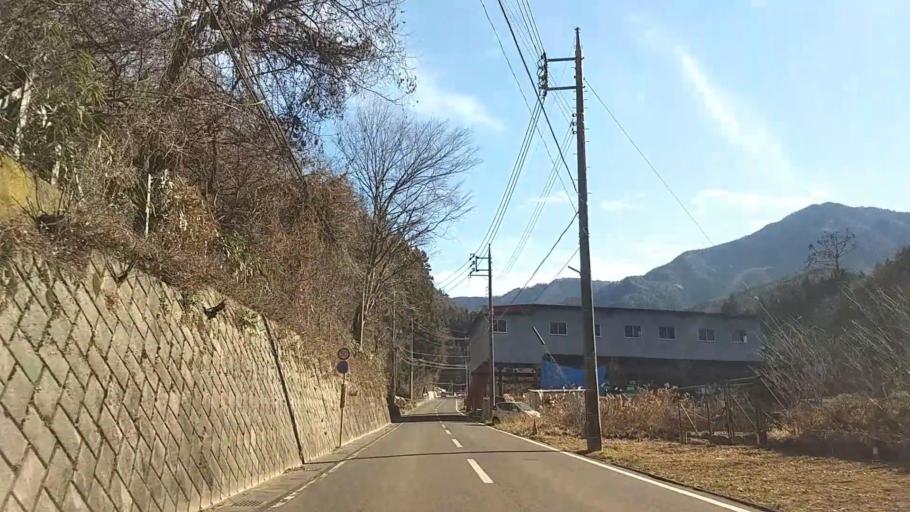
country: JP
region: Yamanashi
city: Otsuki
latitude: 35.5253
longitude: 138.9241
